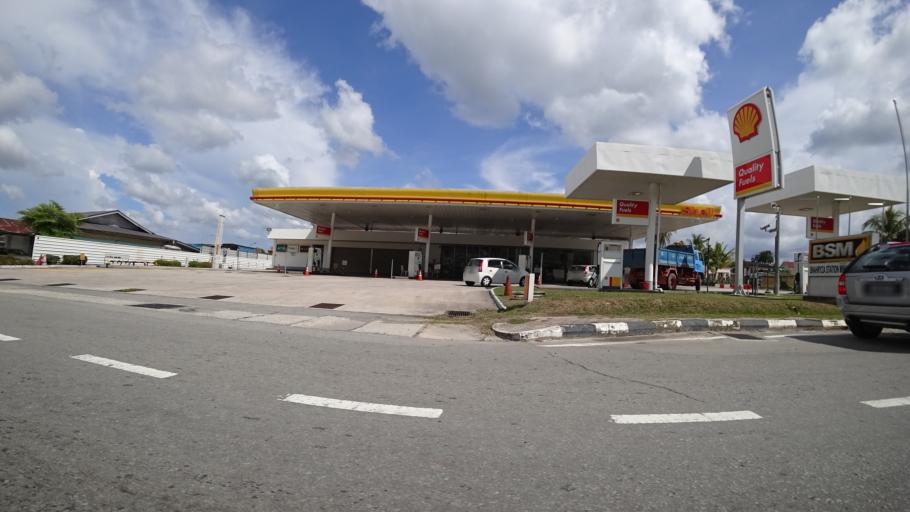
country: BN
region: Brunei and Muara
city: Bandar Seri Begawan
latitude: 4.8554
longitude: 114.8904
